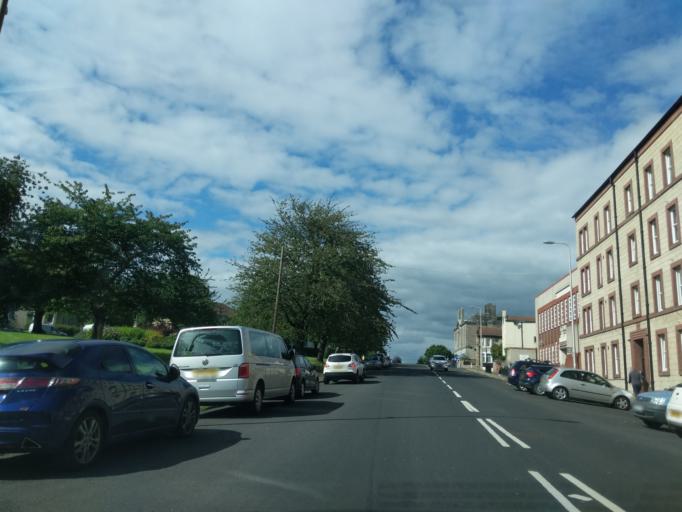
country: GB
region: Scotland
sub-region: West Lothian
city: Seafield
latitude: 55.9599
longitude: -3.1510
